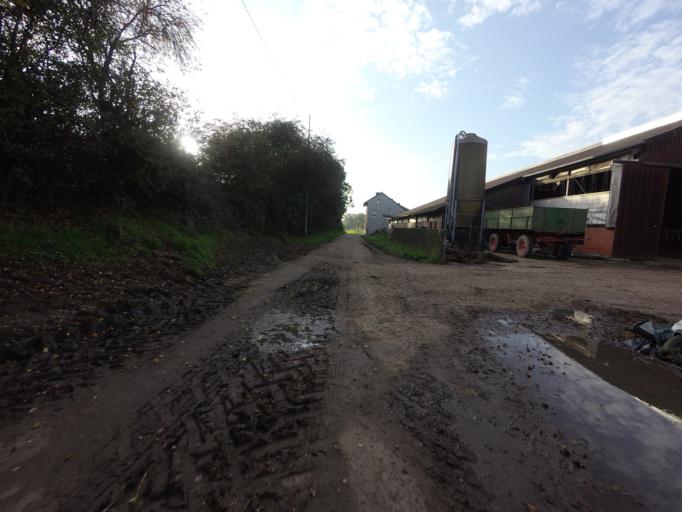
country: DE
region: North Rhine-Westphalia
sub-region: Regierungsbezirk Koln
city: Herzogenrath
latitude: 50.8870
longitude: 6.0964
